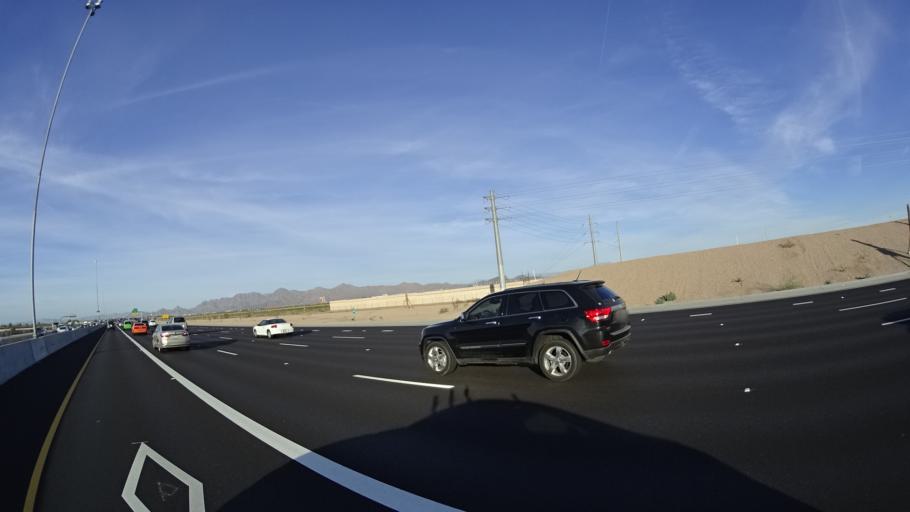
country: US
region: Arizona
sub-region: Maricopa County
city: Scottsdale
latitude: 33.5166
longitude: -111.8884
